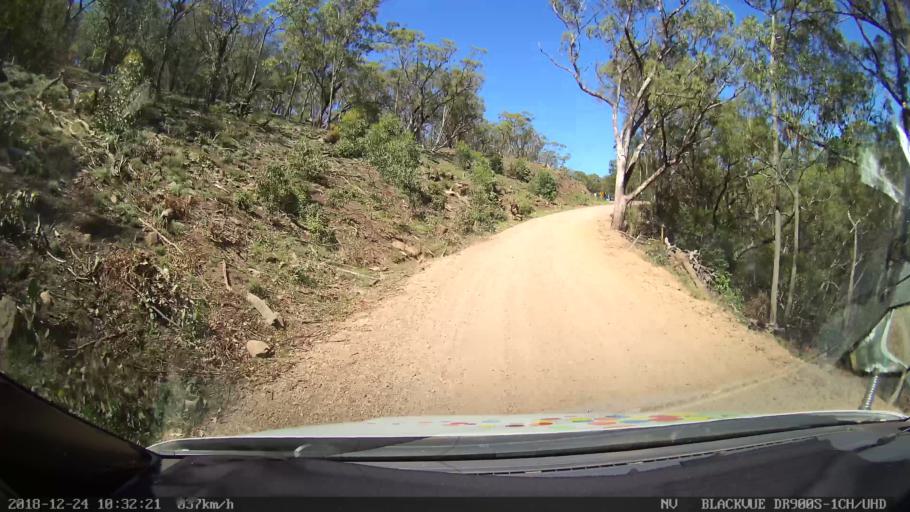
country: AU
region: New South Wales
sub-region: Upper Hunter Shire
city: Merriwa
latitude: -31.8412
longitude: 150.5166
